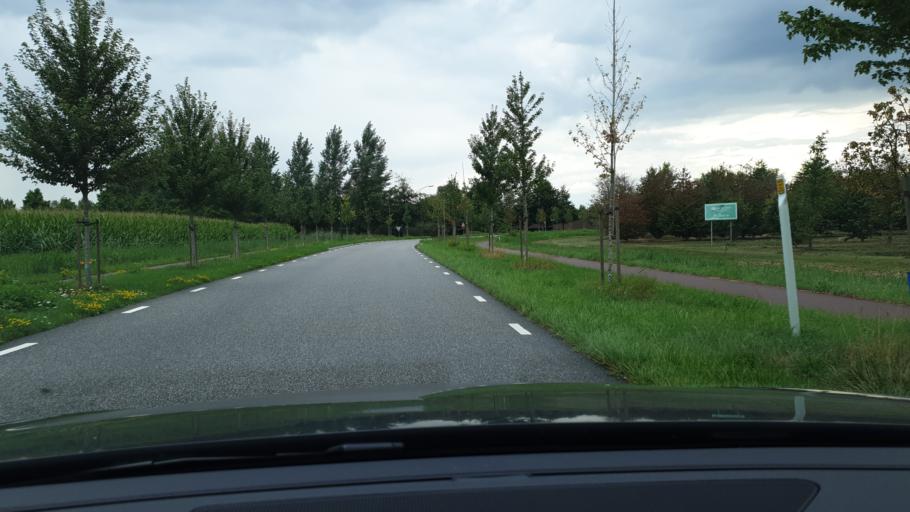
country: NL
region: North Brabant
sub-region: Gemeente Best
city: Best
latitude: 51.5399
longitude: 5.4175
